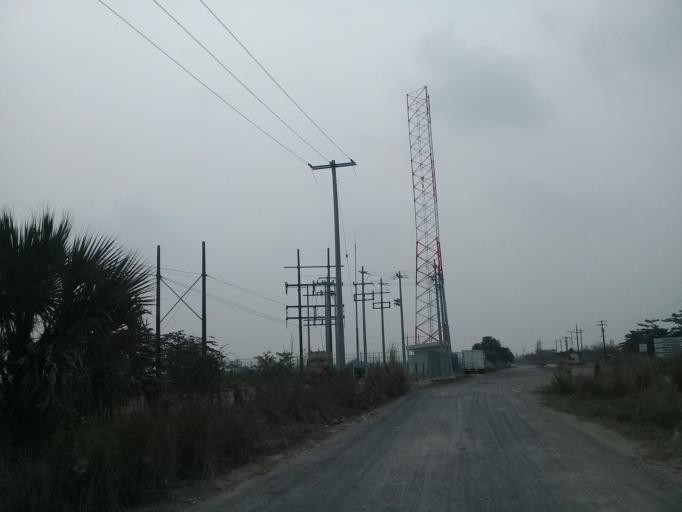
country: MX
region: Veracruz
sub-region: Medellin
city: La Laguna y Monte del Castillo
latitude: 18.9096
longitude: -96.1945
